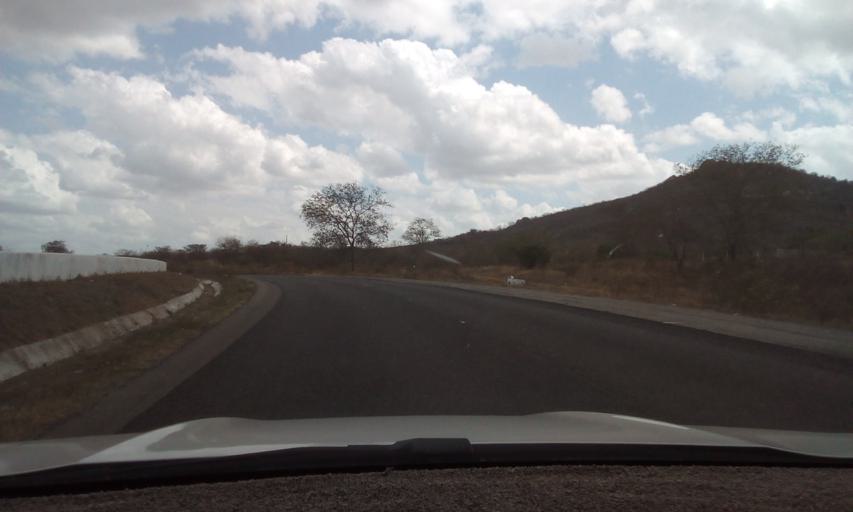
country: BR
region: Pernambuco
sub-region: Toritama
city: Toritama
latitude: -8.0946
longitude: -36.0335
